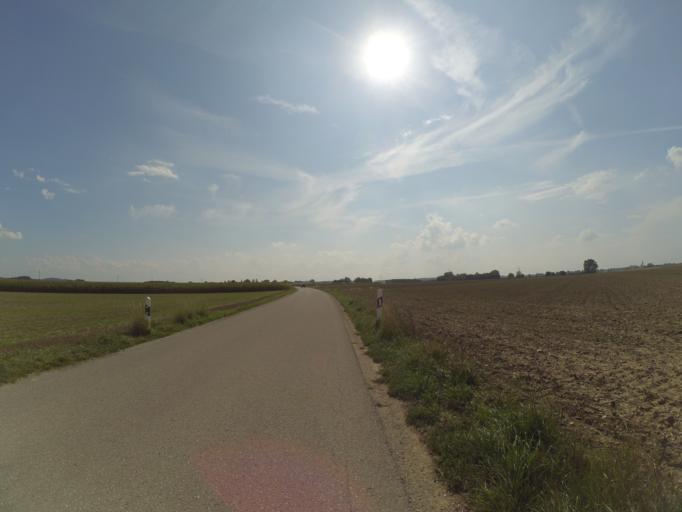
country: DE
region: Bavaria
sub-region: Swabia
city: Lamerdingen
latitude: 48.0970
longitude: 10.7705
